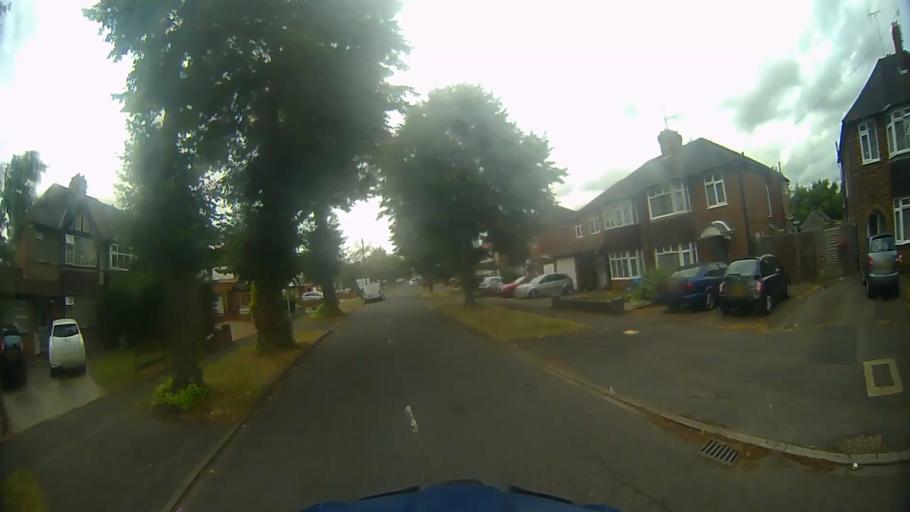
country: GB
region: England
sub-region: Wokingham
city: Earley
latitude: 51.4545
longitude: -0.9319
